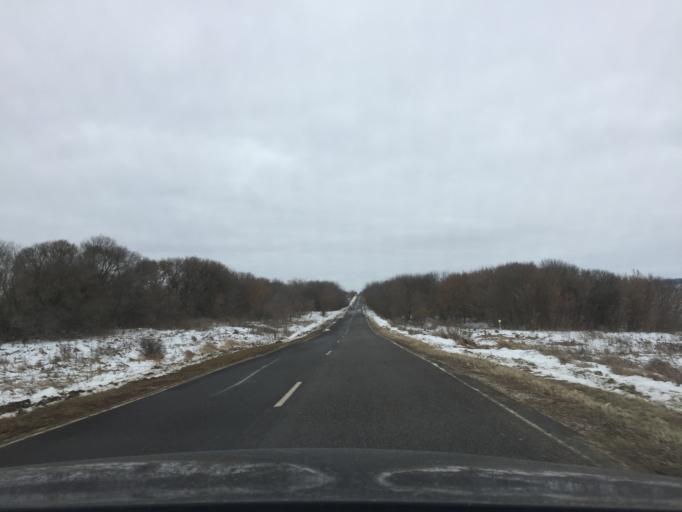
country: RU
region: Tula
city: Teploye
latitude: 53.7945
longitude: 37.6016
